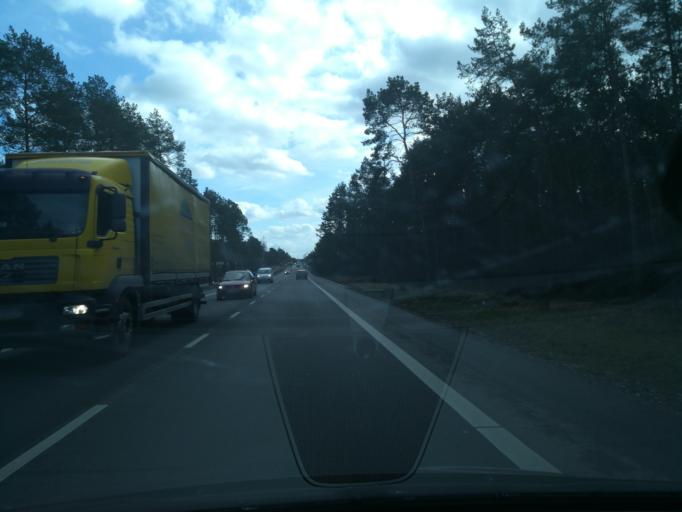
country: PL
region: Kujawsko-Pomorskie
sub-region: Torun
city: Torun
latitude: 52.9801
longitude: 18.6721
